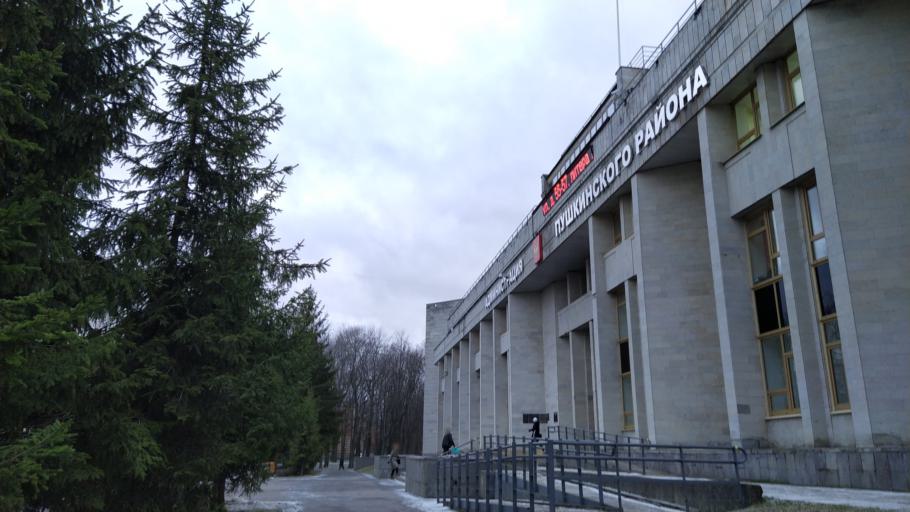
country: RU
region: St.-Petersburg
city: Pushkin
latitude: 59.7222
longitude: 30.4173
